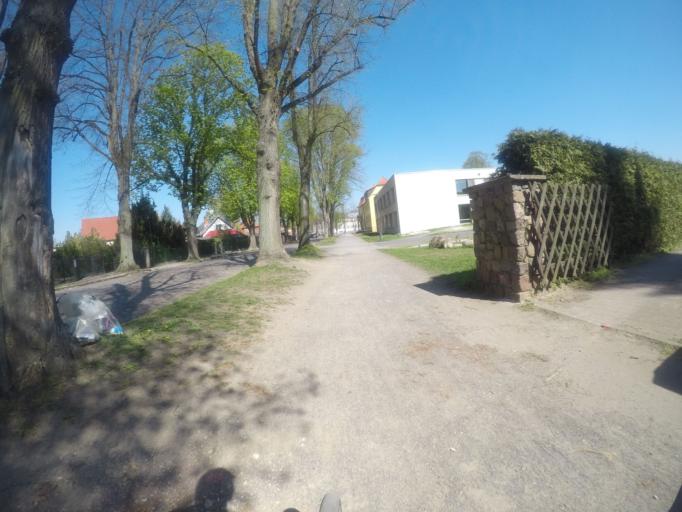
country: DE
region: Berlin
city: Buch
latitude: 52.6547
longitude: 13.5293
